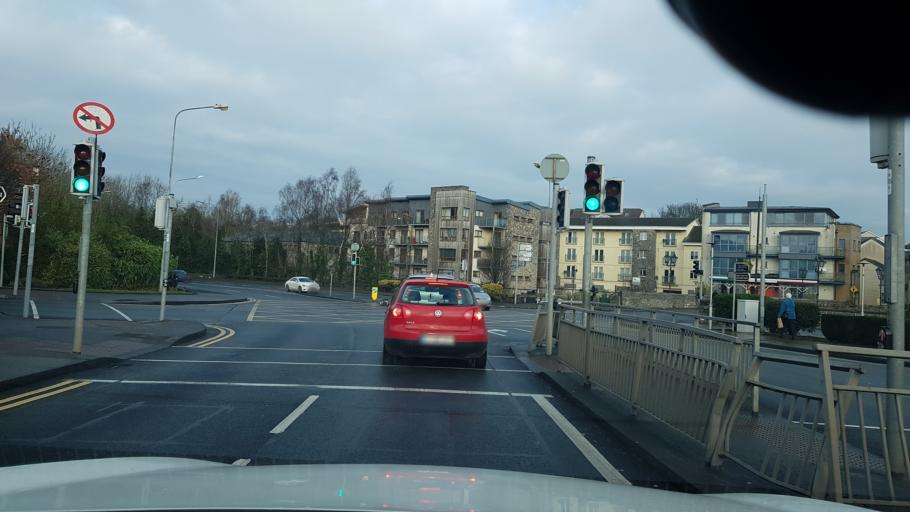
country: IE
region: Leinster
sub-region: An Mhi
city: Navan
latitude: 53.6542
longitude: -6.6823
